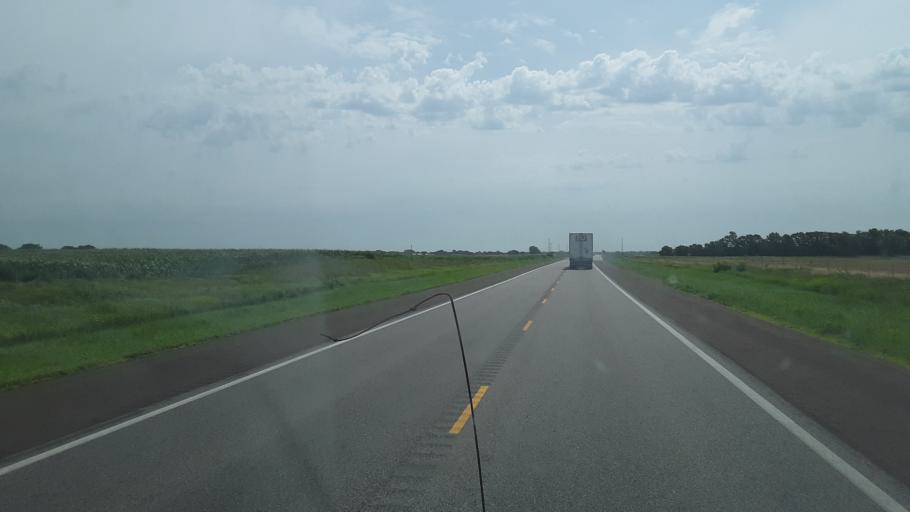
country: US
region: Kansas
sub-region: Reno County
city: South Hutchinson
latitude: 37.9851
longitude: -98.0923
